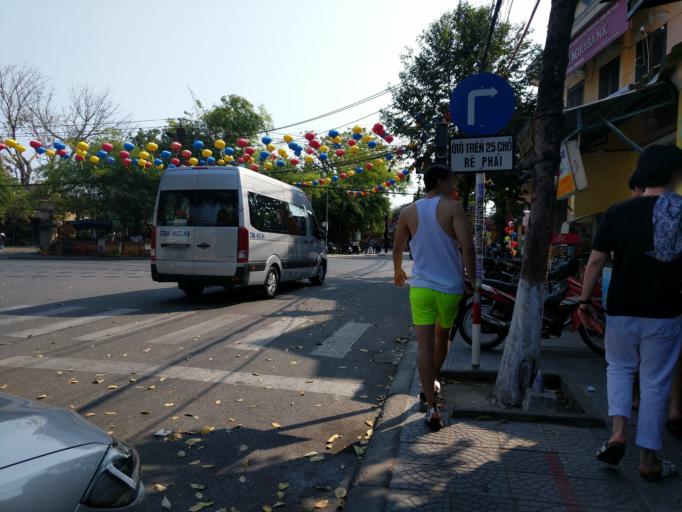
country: VN
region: Quang Nam
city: Hoi An
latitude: 15.8801
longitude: 108.3288
